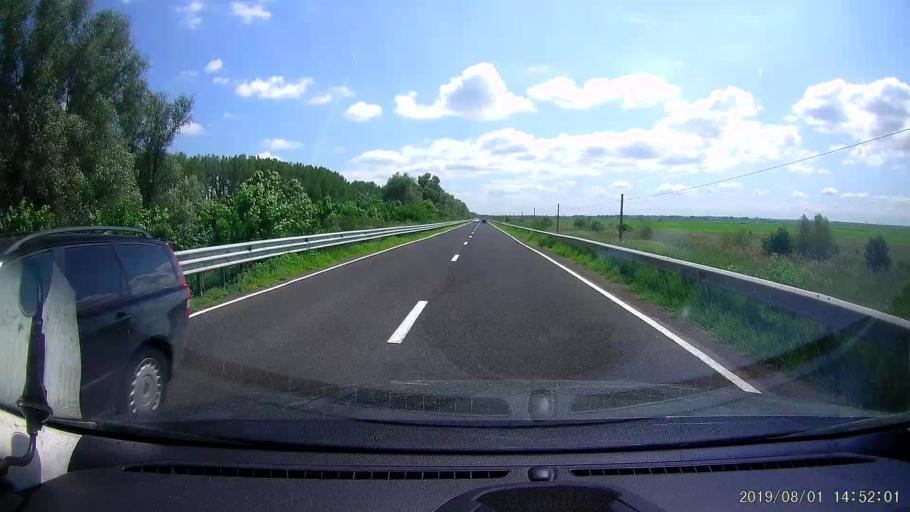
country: RO
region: Braila
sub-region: Comuna Vadeni
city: Vadeni
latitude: 45.3643
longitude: 28.0136
